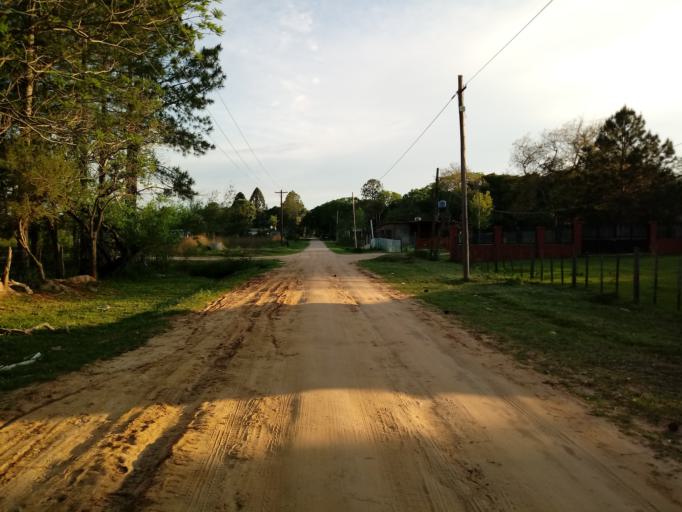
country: AR
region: Corrientes
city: San Luis del Palmar
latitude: -27.4539
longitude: -58.6577
